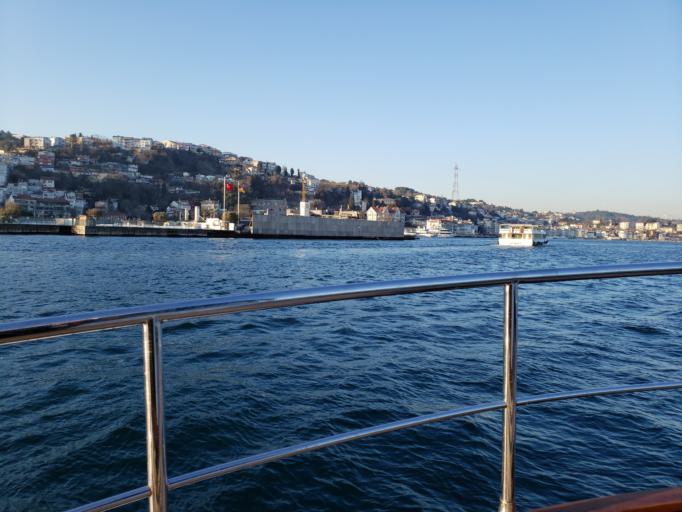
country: TR
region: Istanbul
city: UEskuedar
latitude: 41.0583
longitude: 29.0403
